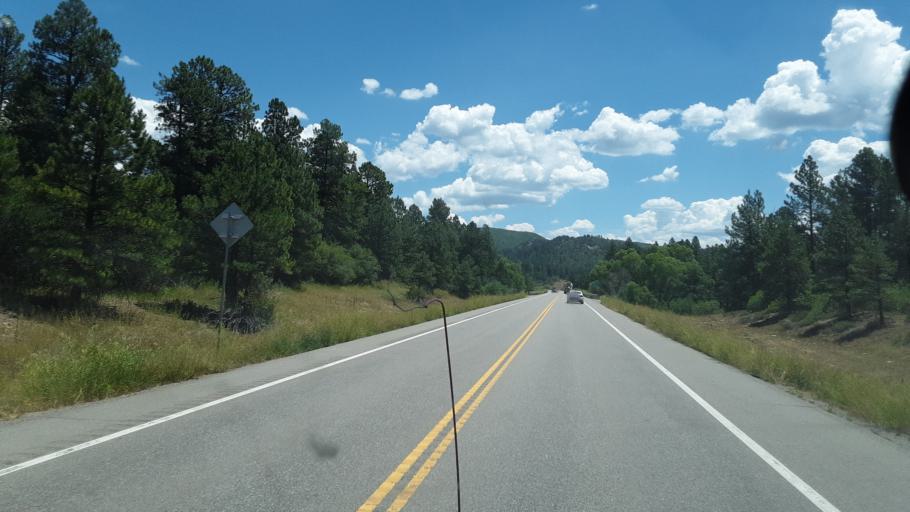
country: US
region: Colorado
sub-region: La Plata County
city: Bayfield
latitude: 37.2853
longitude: -107.4921
